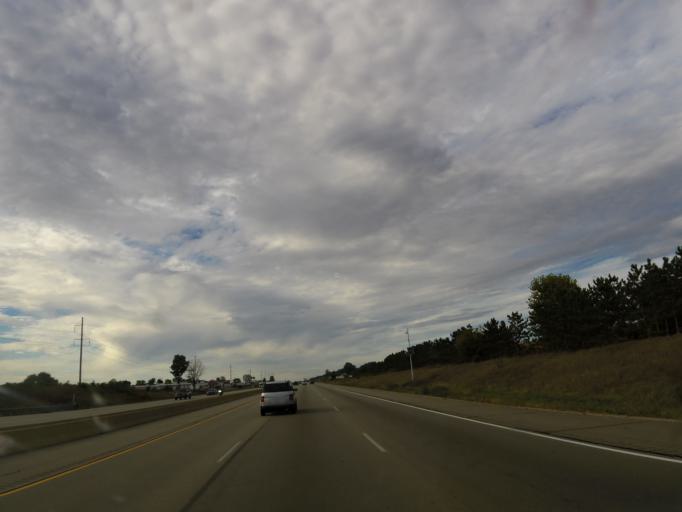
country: US
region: Wisconsin
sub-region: Dane County
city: Windsor
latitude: 43.1650
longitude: -89.3122
